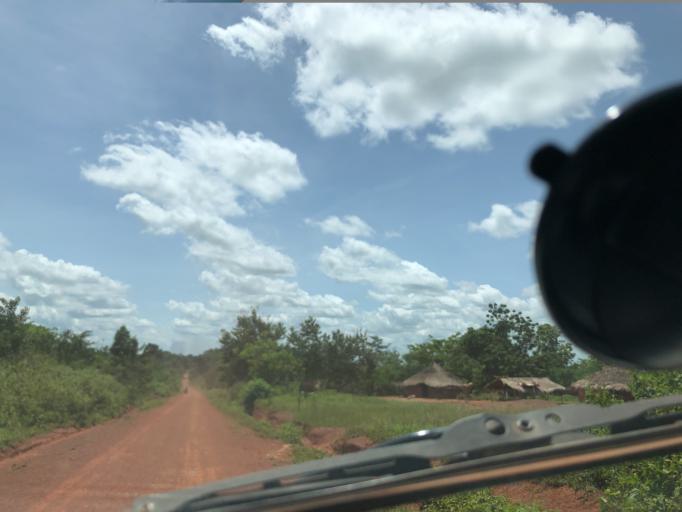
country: CD
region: Equateur
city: Libenge
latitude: 3.6927
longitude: 19.0937
